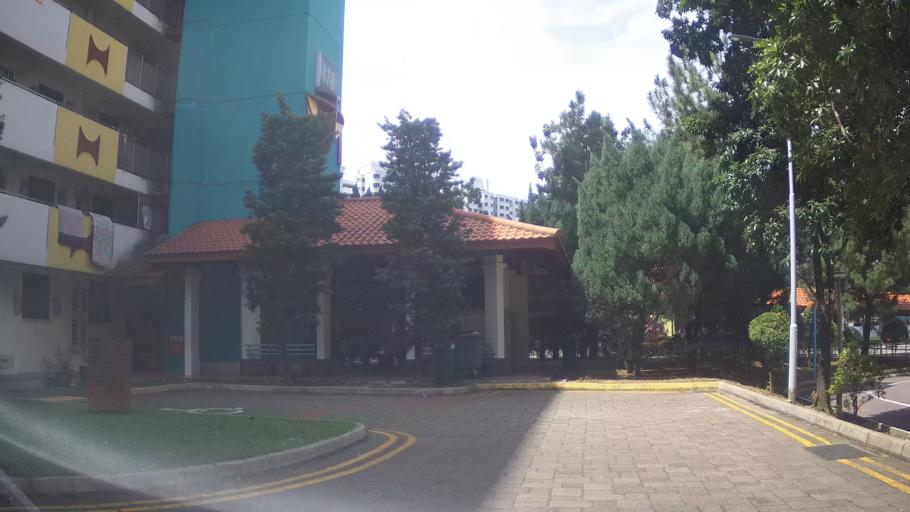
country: MY
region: Johor
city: Johor Bahru
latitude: 1.3355
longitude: 103.7229
